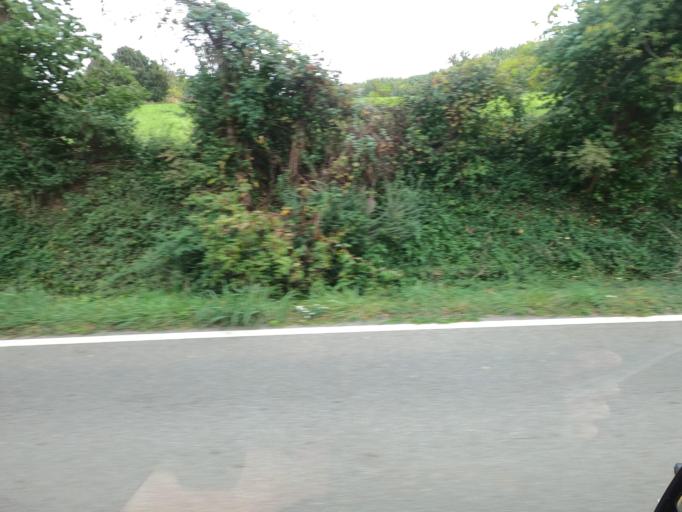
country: US
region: Tennessee
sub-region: Washington County
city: Jonesborough
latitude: 36.2452
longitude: -82.5524
